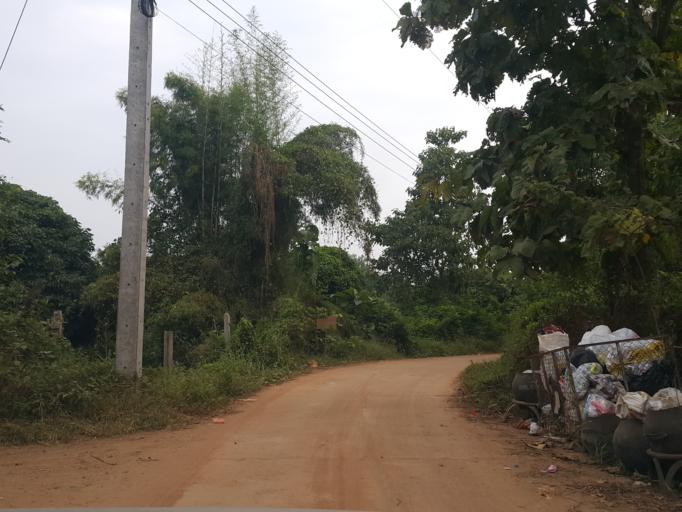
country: TH
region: Mae Hong Son
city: Wiang Nuea
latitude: 19.3758
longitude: 98.4518
